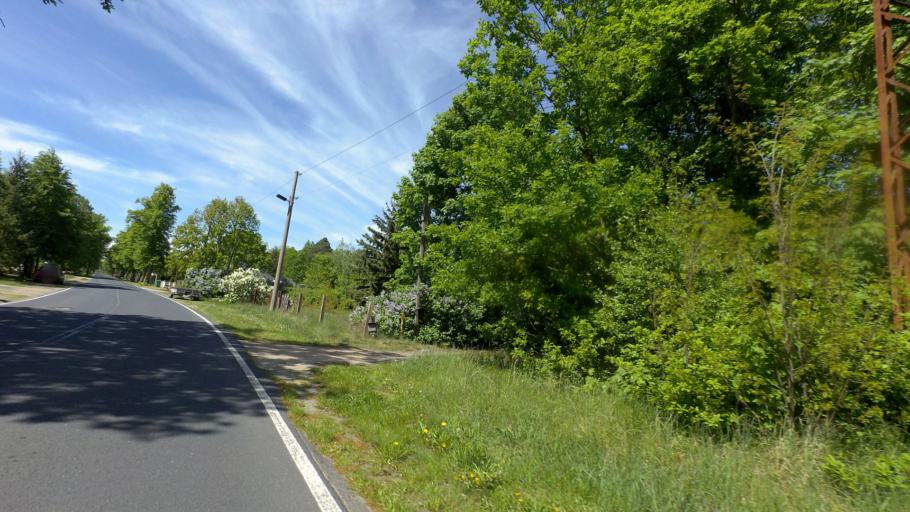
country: DE
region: Brandenburg
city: Baruth
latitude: 52.0612
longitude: 13.5041
